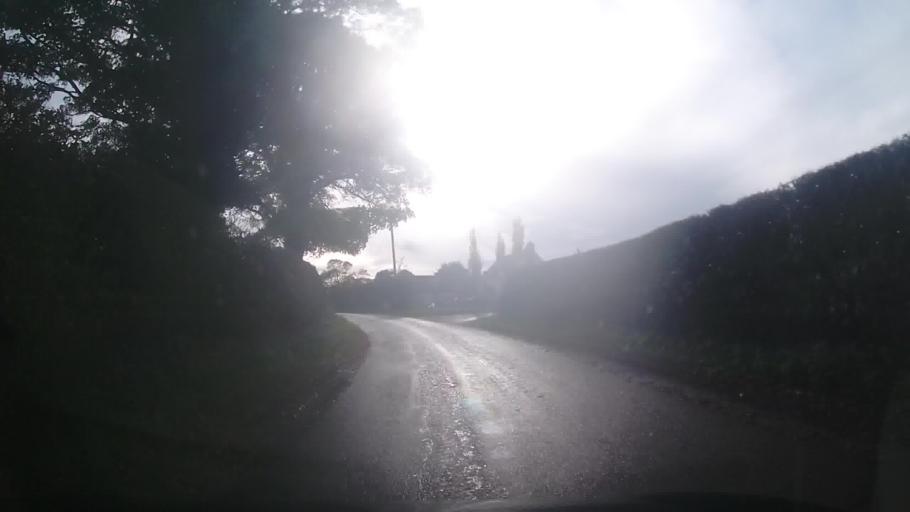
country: GB
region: England
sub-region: Shropshire
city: Whitchurch
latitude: 52.9557
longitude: -2.6960
